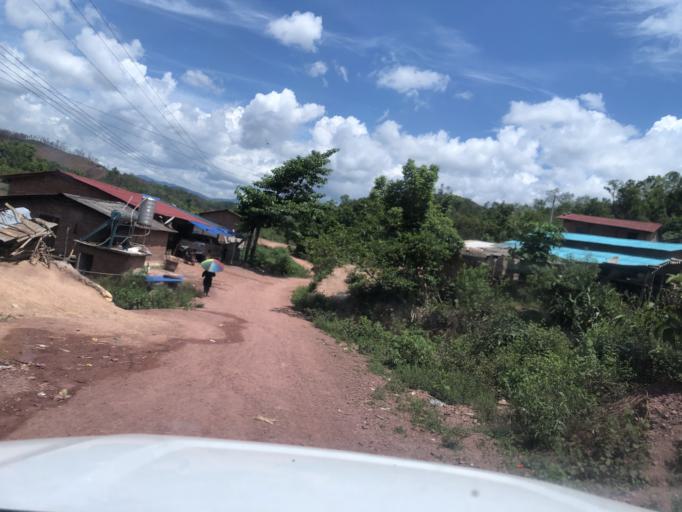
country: CN
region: Yunnan
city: Menglie
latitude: 22.2471
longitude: 101.6081
